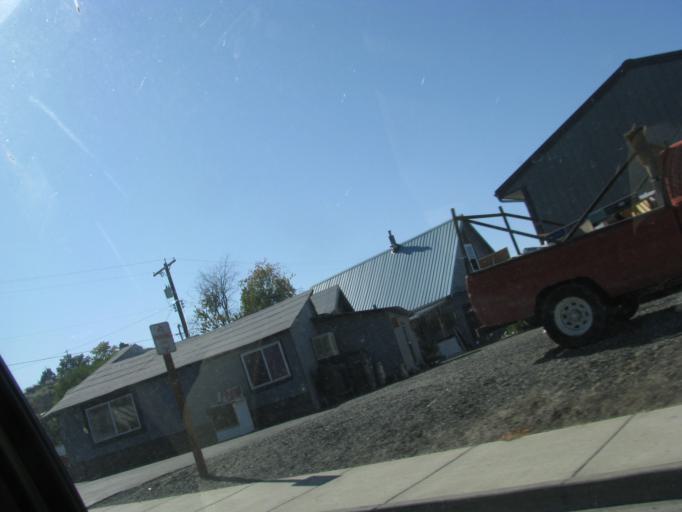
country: US
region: Washington
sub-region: Asotin County
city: Asotin
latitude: 46.3402
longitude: -117.0487
